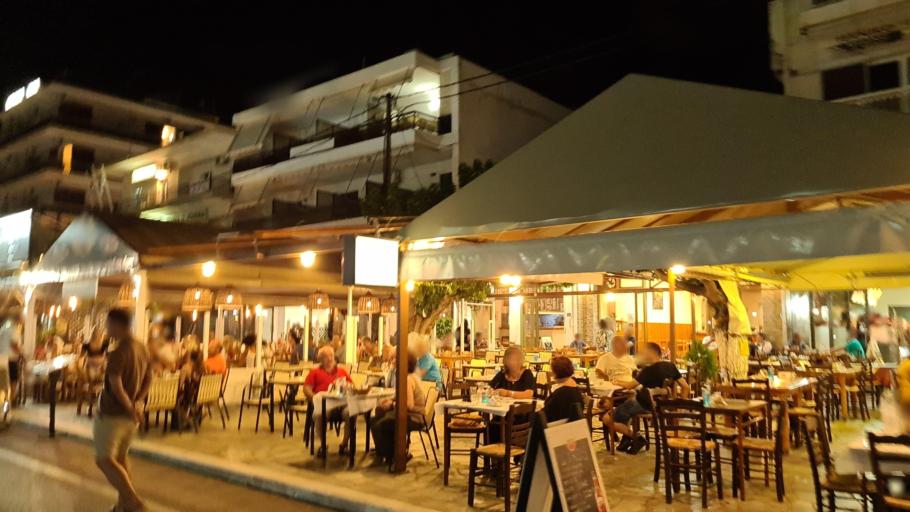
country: GR
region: Central Greece
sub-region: Nomos Evvoias
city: Karystos
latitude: 38.0132
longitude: 24.4190
